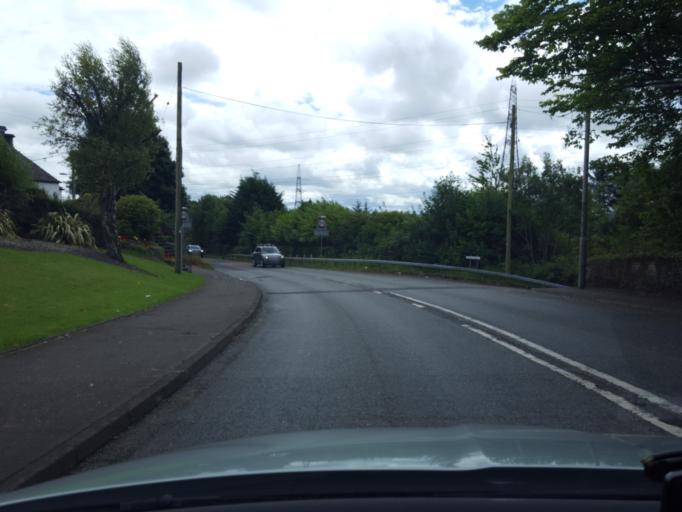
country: GB
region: Scotland
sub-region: Stirling
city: Cowie
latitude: 56.0564
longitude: -3.8684
